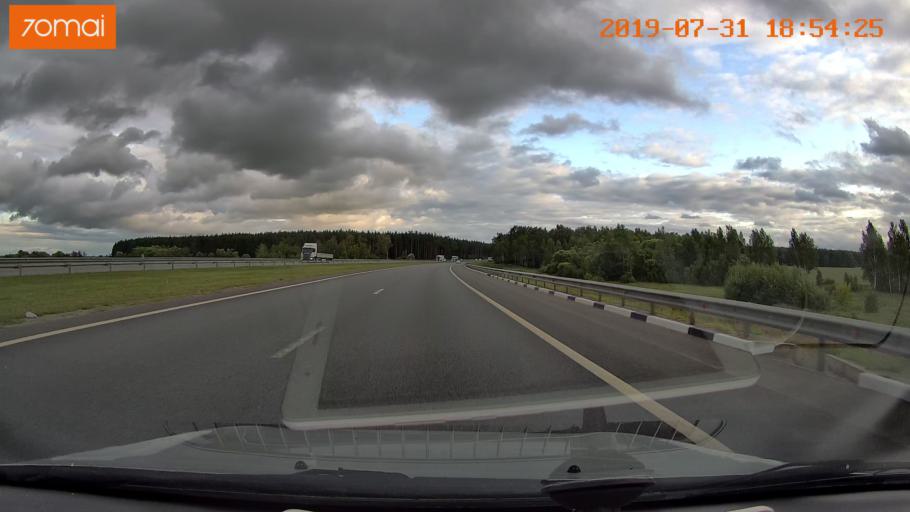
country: RU
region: Moskovskaya
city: Raduzhnyy
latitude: 55.1902
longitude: 38.6681
